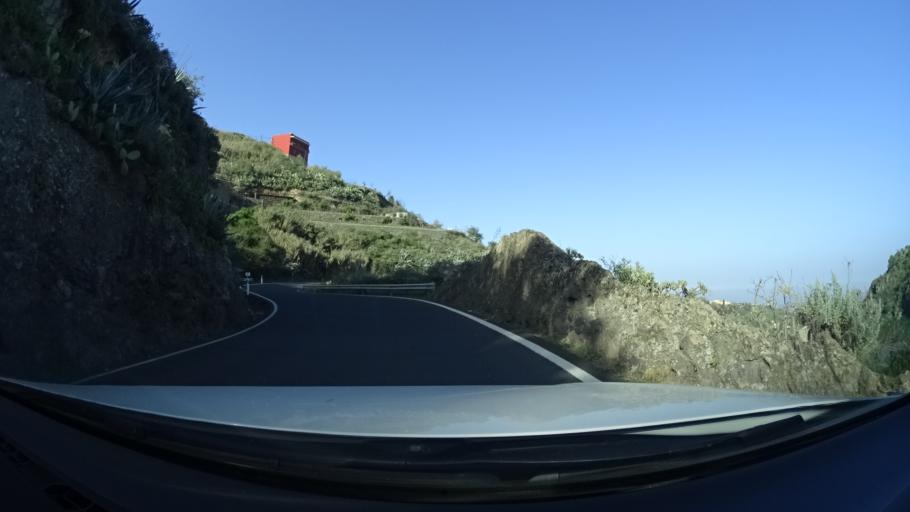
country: ES
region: Canary Islands
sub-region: Provincia de Las Palmas
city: Valleseco
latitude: 28.0260
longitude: -15.5559
